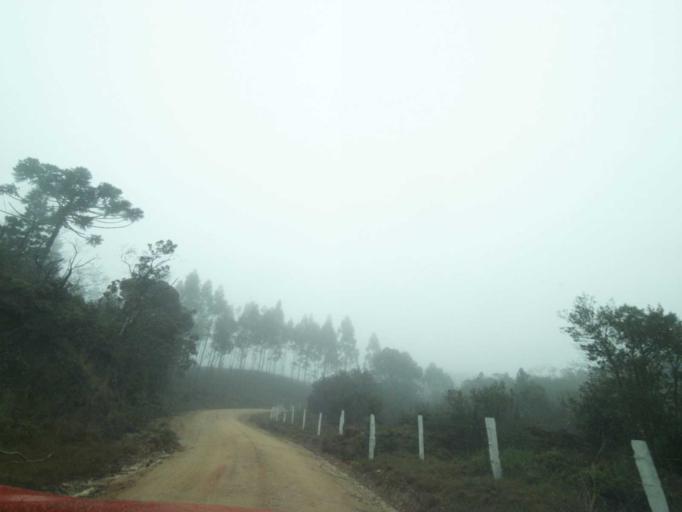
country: BR
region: Santa Catarina
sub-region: Anitapolis
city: Anitapolis
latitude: -27.9054
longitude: -49.1634
